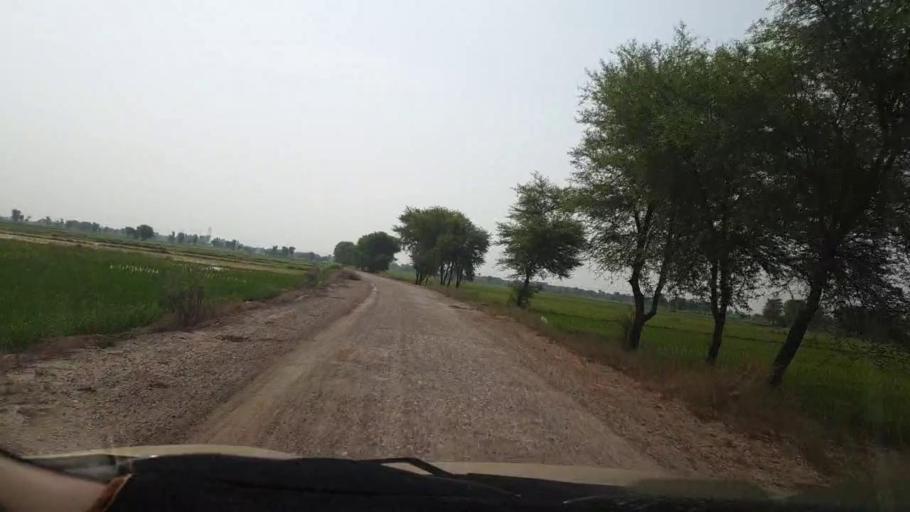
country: PK
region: Sindh
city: Goth Garelo
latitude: 27.4392
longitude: 68.0384
